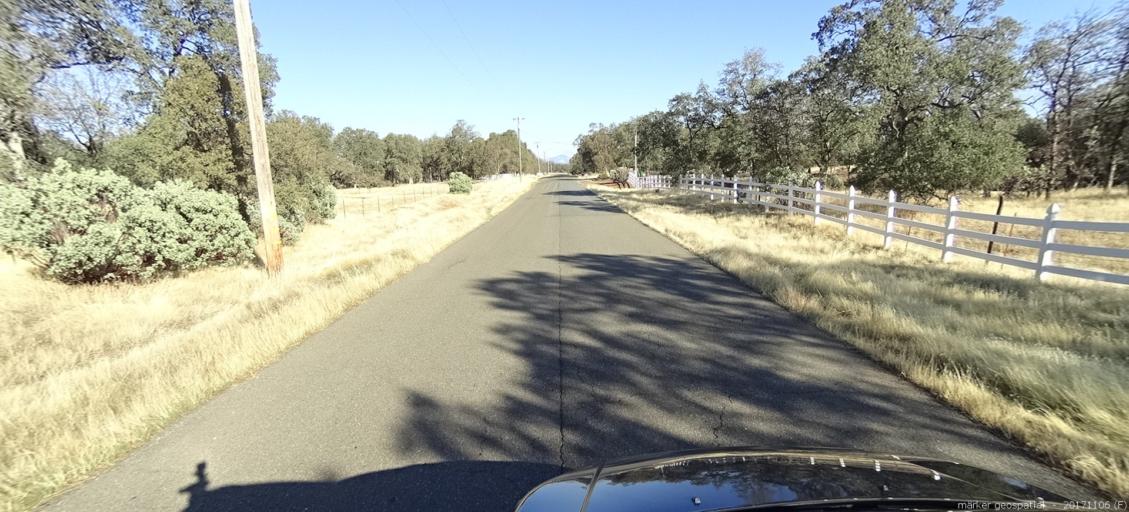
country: US
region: California
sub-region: Shasta County
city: Palo Cedro
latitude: 40.5119
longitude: -122.2482
